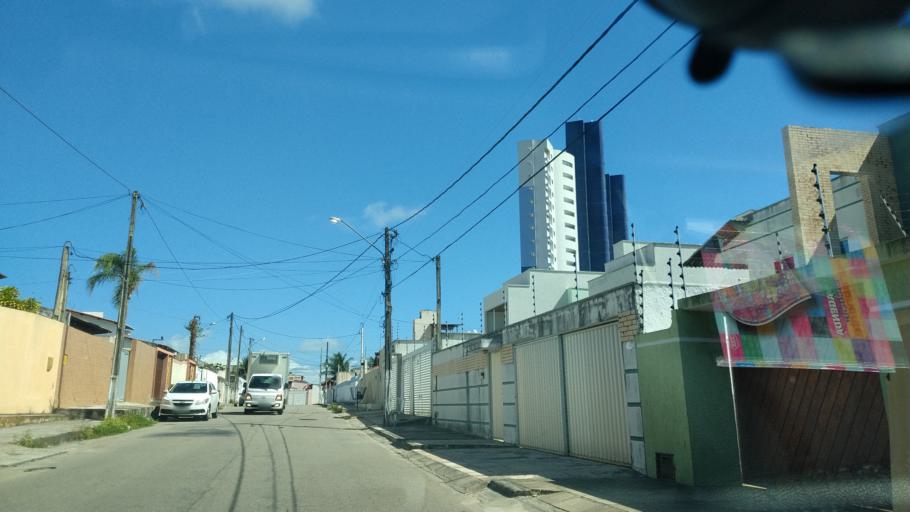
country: BR
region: Rio Grande do Norte
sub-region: Natal
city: Natal
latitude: -5.8708
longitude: -35.1910
